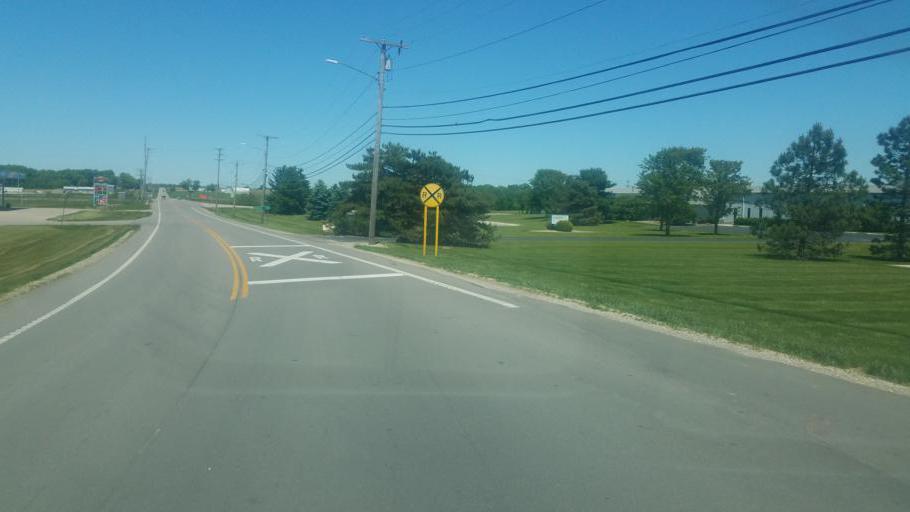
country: US
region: Ohio
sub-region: Darke County
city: Versailles
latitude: 40.2241
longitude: -84.4649
